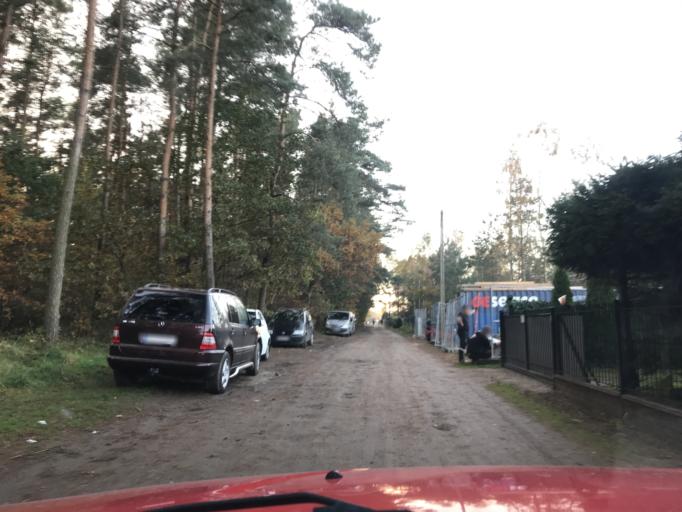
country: PL
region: Greater Poland Voivodeship
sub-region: Powiat poznanski
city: Dopiewo
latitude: 52.3898
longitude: 16.7275
